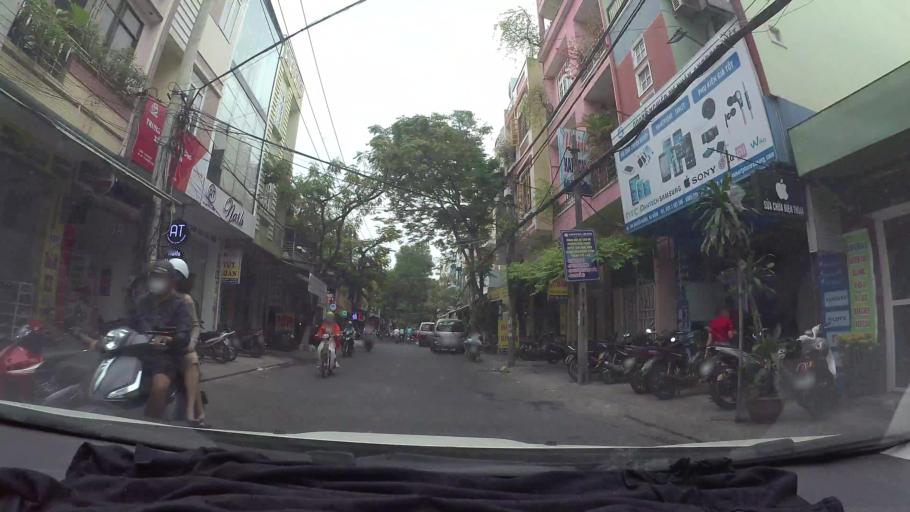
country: VN
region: Da Nang
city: Da Nang
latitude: 16.0597
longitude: 108.2134
